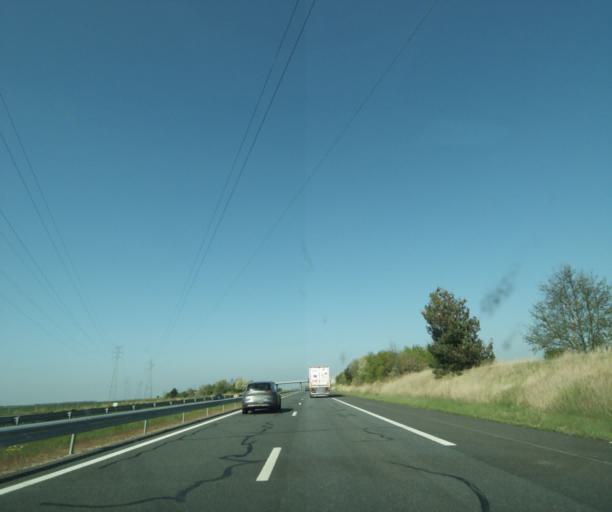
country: FR
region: Centre
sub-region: Departement du Loiret
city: Corquilleroy
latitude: 48.0718
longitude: 2.6769
